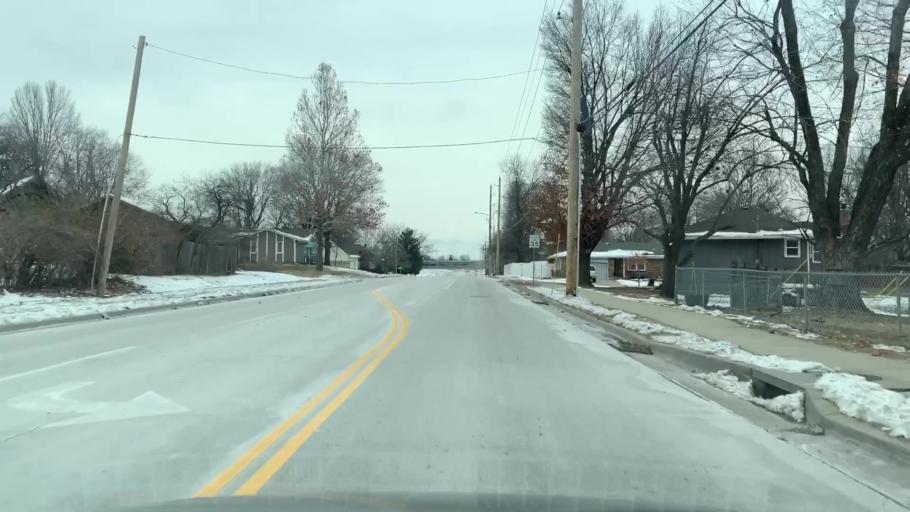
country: US
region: Missouri
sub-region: Jackson County
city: Lees Summit
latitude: 38.9407
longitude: -94.3644
